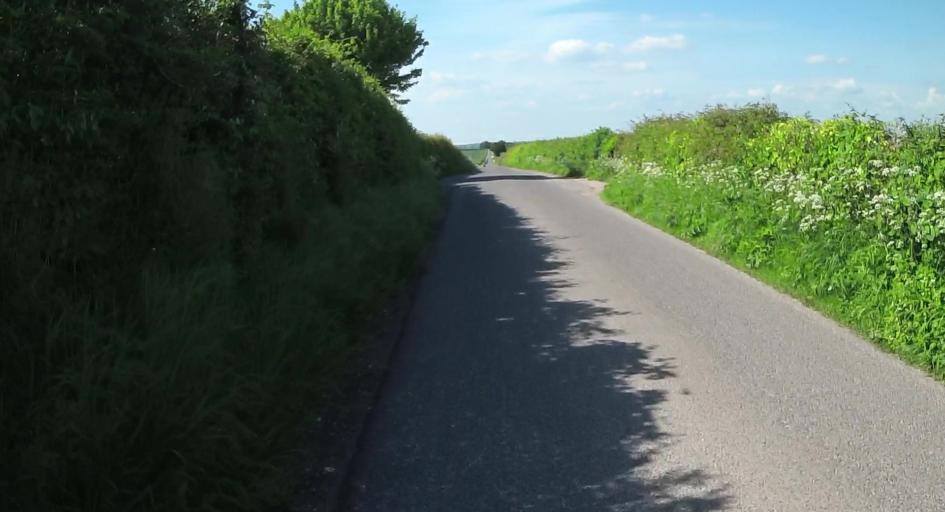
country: GB
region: England
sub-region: Hampshire
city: Kings Worthy
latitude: 51.0715
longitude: -1.2759
